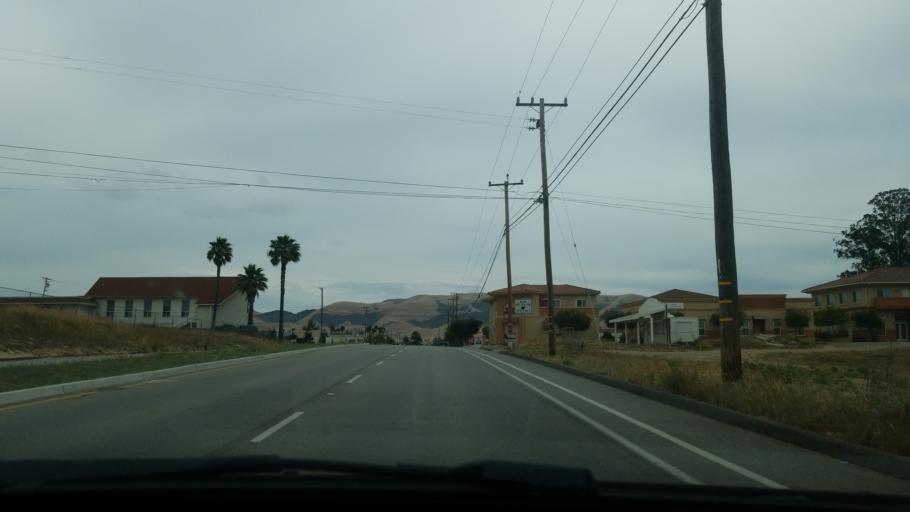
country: US
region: California
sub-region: San Luis Obispo County
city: Nipomo
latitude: 35.0334
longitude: -120.4906
